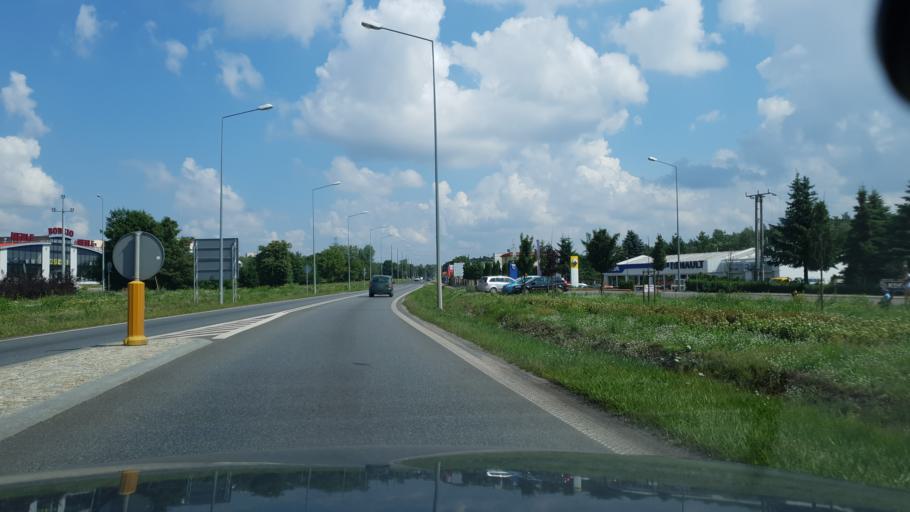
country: PL
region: Kujawsko-Pomorskie
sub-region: Grudziadz
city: Grudziadz
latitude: 53.4473
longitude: 18.7284
